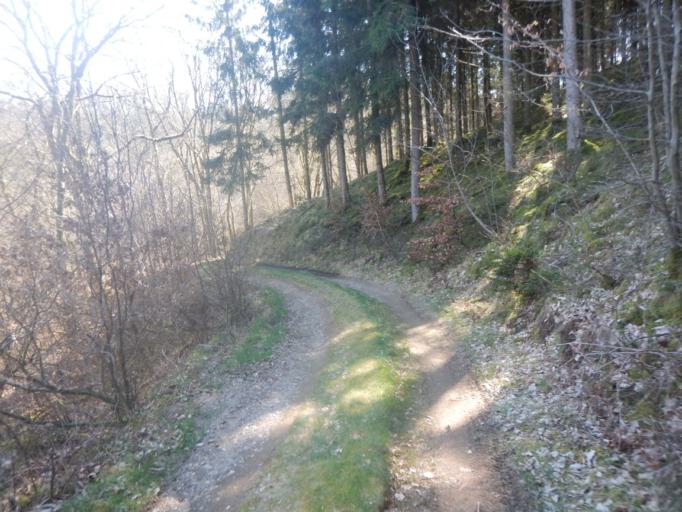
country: LU
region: Diekirch
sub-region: Canton de Wiltz
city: Goesdorf
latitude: 49.9550
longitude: 5.9676
